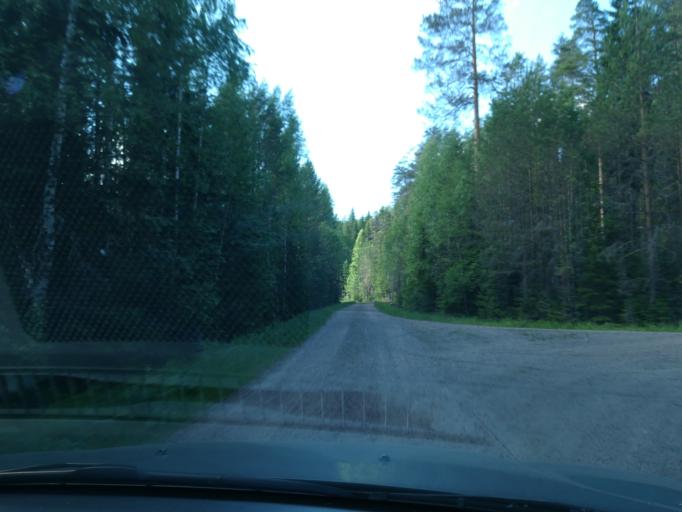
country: FI
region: South Karelia
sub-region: Imatra
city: Ruokolahti
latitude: 61.5438
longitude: 28.8059
